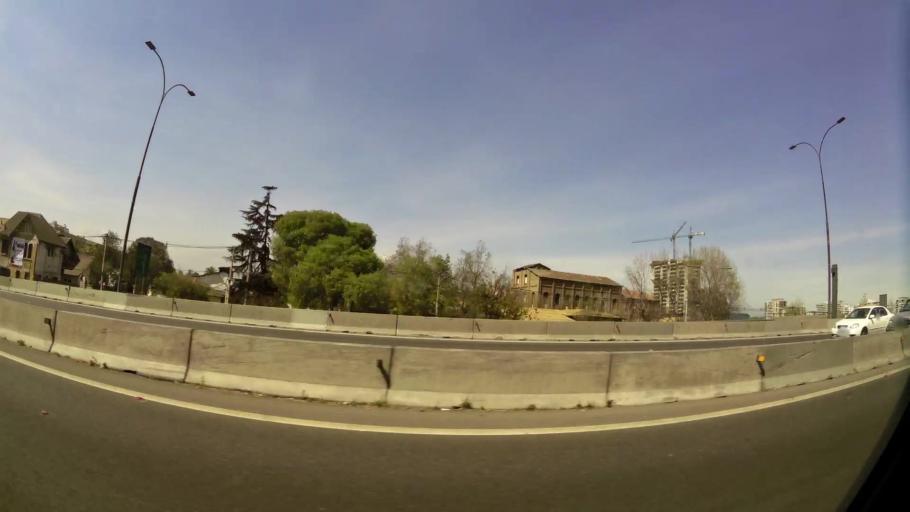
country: CL
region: Santiago Metropolitan
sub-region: Provincia de Santiago
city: Santiago
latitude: -33.4754
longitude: -70.6546
